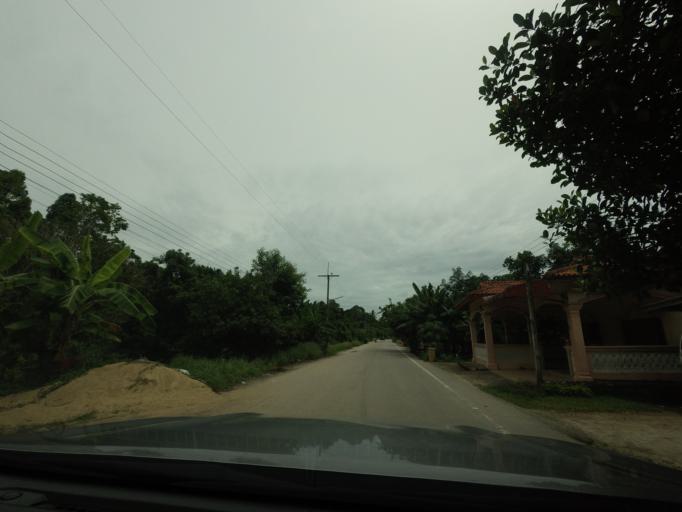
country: TH
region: Pattani
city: Sai Buri
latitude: 6.6539
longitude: 101.5535
